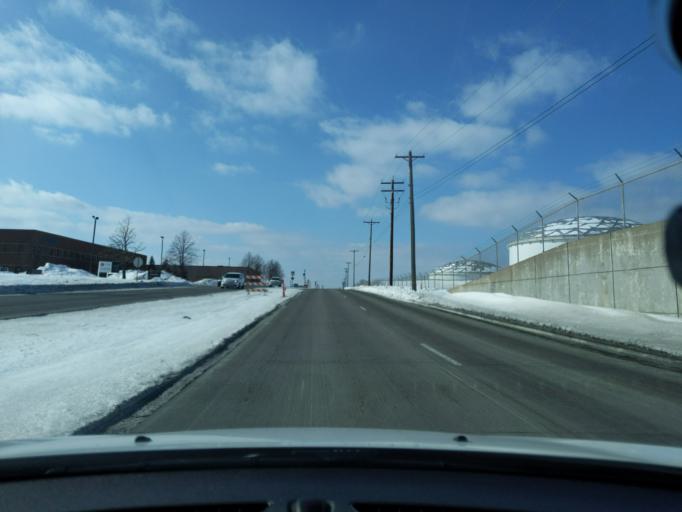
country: US
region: Minnesota
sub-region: Hennepin County
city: Saint Anthony
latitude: 45.0207
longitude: -93.1986
